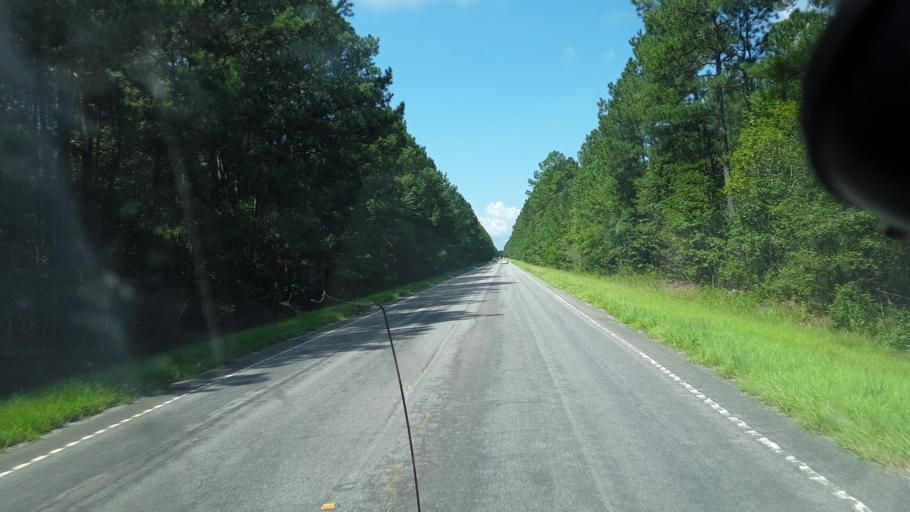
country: US
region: South Carolina
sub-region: Berkeley County
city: Saint Stephen
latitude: 33.2871
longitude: -79.8435
